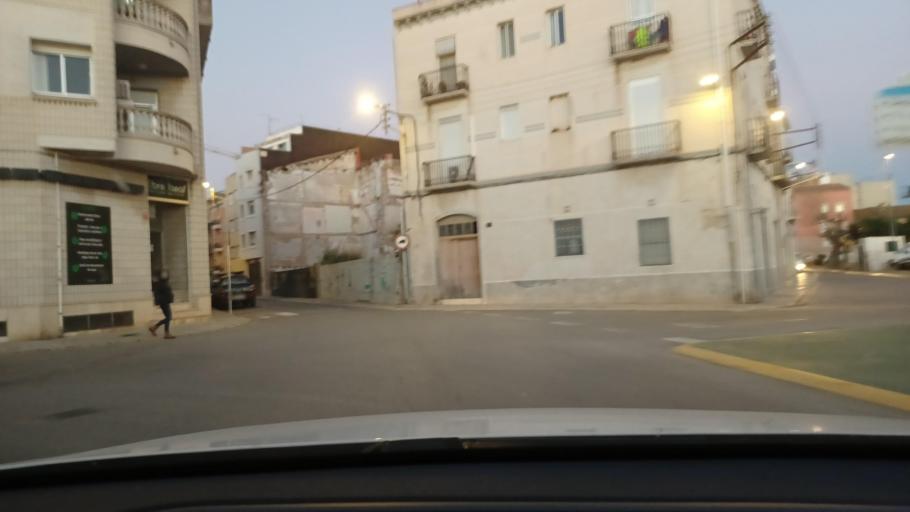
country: ES
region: Catalonia
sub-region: Provincia de Tarragona
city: Amposta
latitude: 40.7129
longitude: 0.5833
